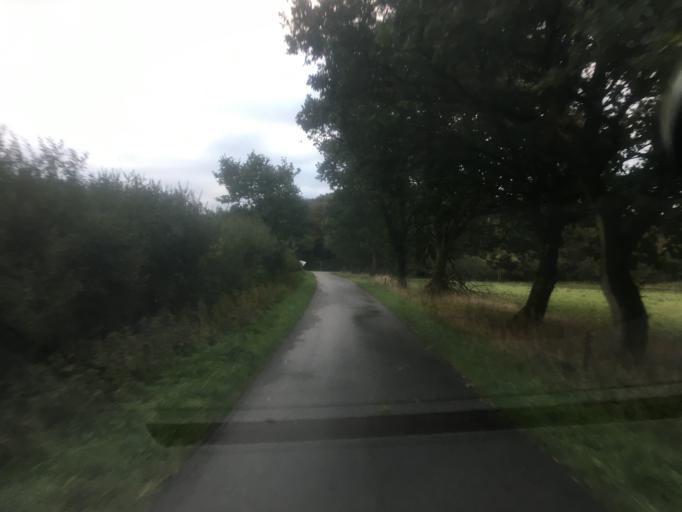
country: DK
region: South Denmark
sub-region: Tonder Kommune
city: Logumkloster
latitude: 55.0214
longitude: 8.9656
